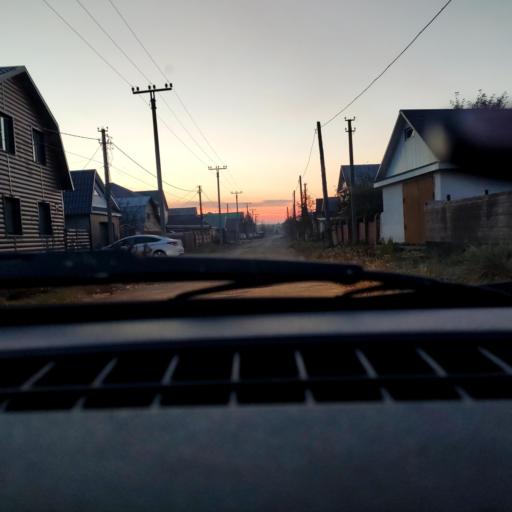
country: RU
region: Bashkortostan
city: Iglino
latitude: 54.8356
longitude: 56.1812
